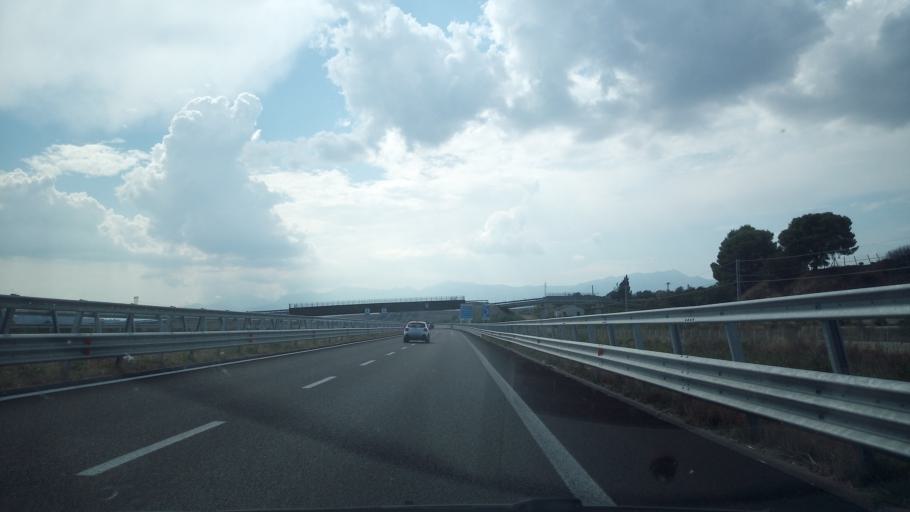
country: IT
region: Calabria
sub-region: Provincia di Cosenza
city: Doria
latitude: 39.7271
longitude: 16.3310
